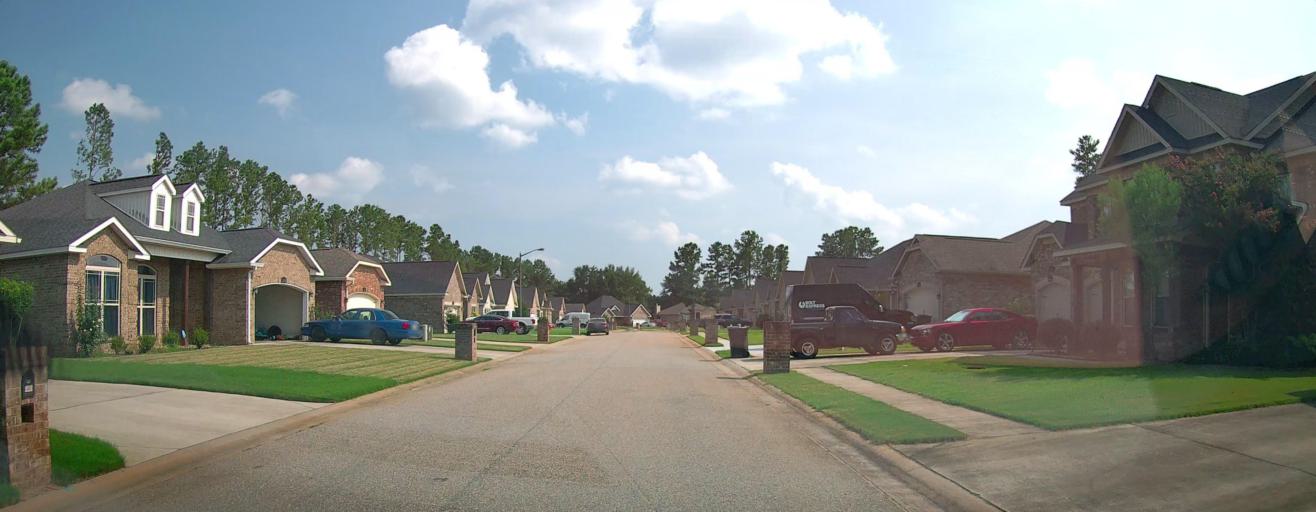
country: US
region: Georgia
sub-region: Houston County
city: Centerville
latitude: 32.6489
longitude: -83.7056
